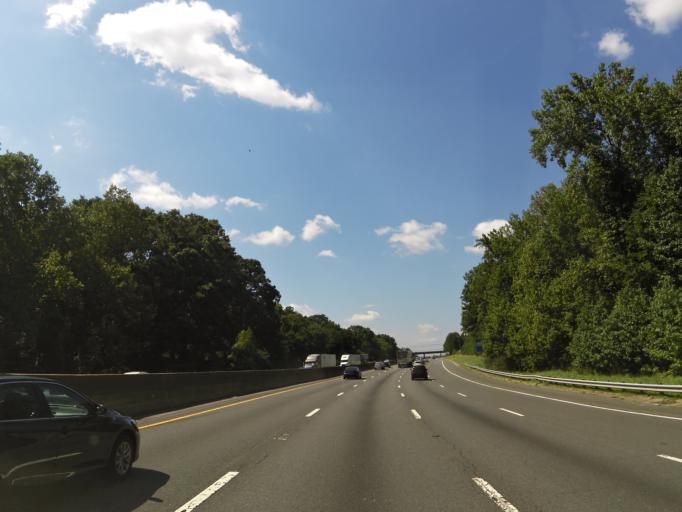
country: US
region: North Carolina
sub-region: Gaston County
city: Gastonia
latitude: 35.2741
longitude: -81.1626
